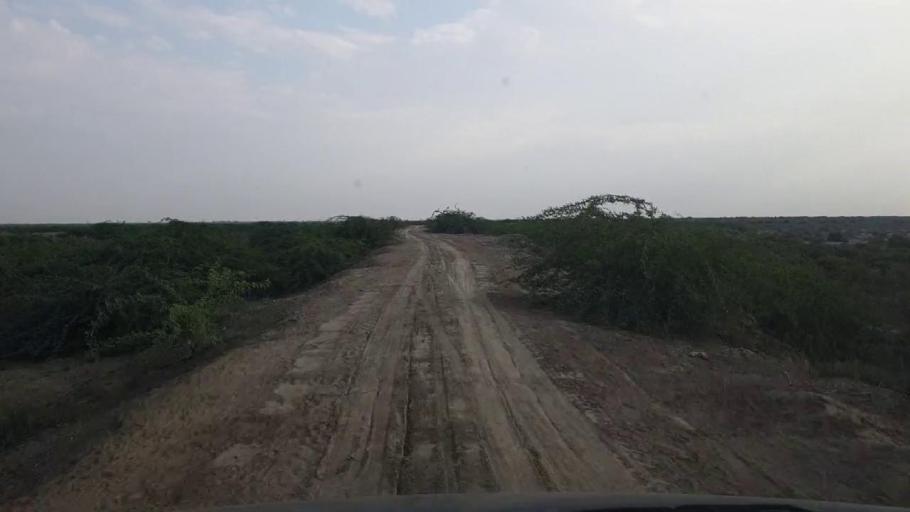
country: PK
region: Sindh
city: Badin
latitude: 24.4789
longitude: 68.6993
